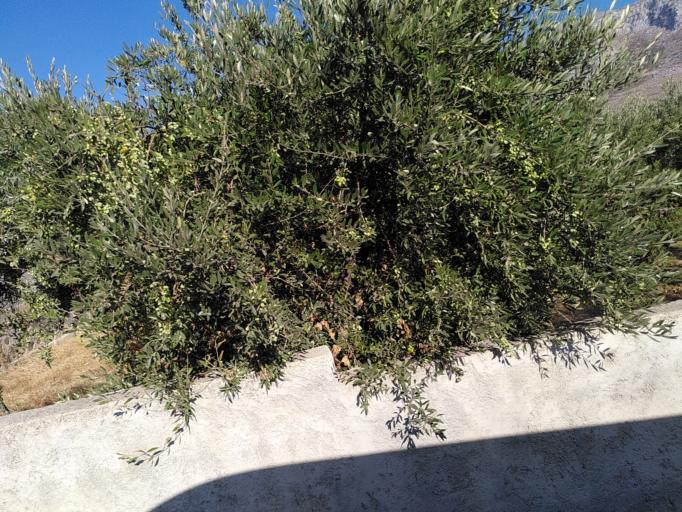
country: GR
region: South Aegean
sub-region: Nomos Kykladon
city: Amorgos
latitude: 36.9081
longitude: 25.9782
